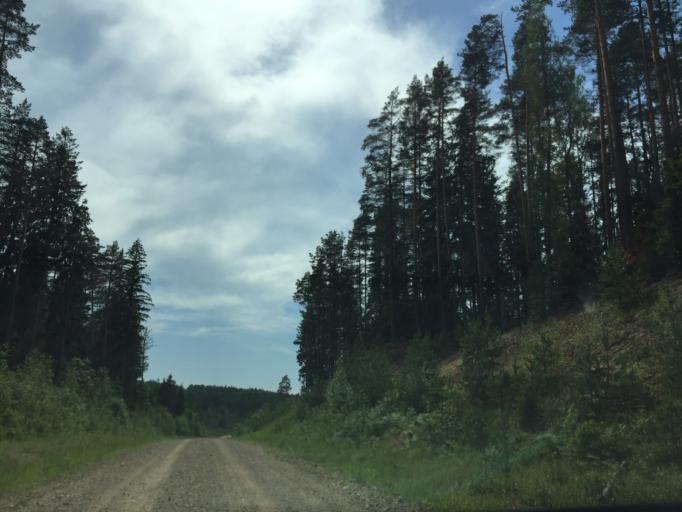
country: LV
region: Engure
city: Smarde
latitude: 57.0206
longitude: 23.2706
